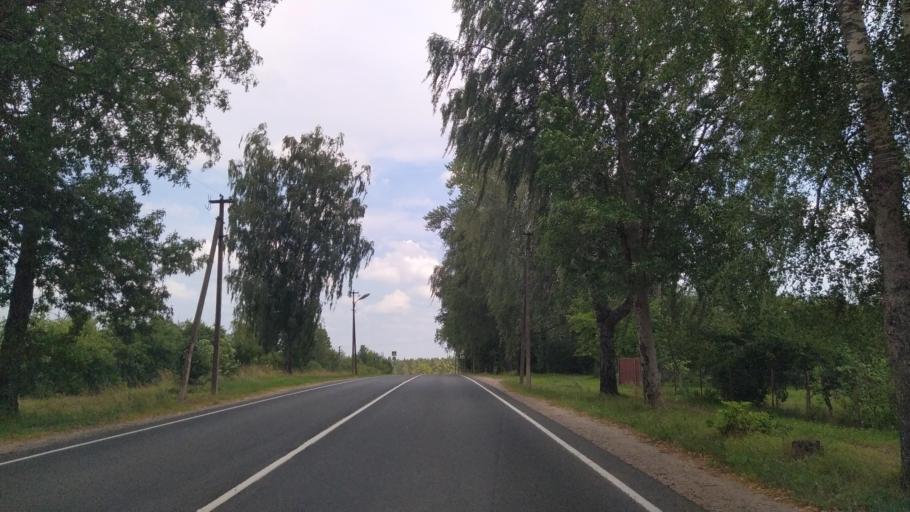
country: RU
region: Pskov
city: Pskov
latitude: 57.7609
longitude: 28.7648
